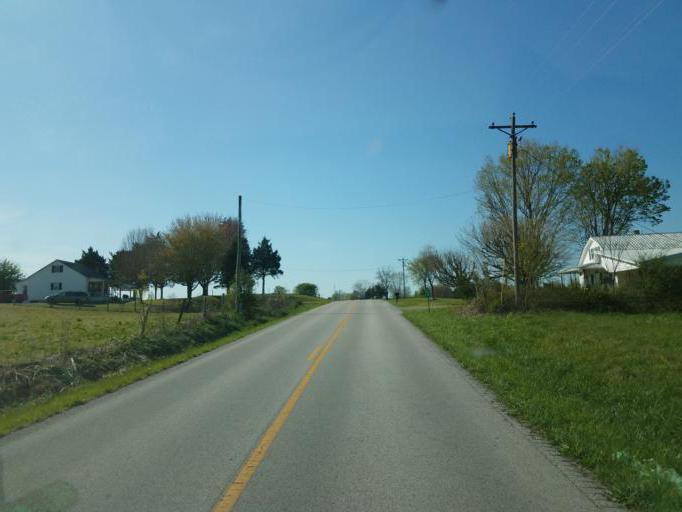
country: US
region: Kentucky
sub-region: Edmonson County
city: Brownsville
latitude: 37.1296
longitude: -86.1643
